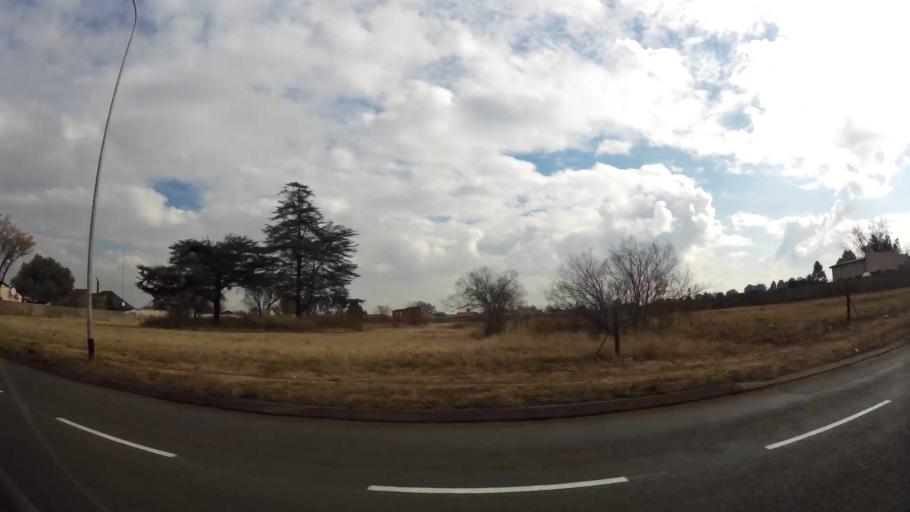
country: ZA
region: Gauteng
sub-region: Sedibeng District Municipality
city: Meyerton
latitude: -26.5901
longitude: 28.0010
